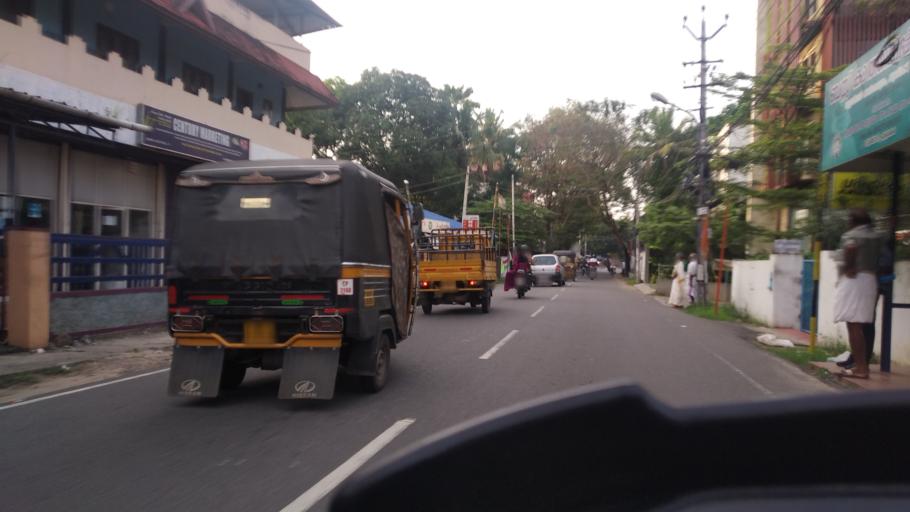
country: IN
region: Kerala
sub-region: Ernakulam
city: Elur
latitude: 10.0128
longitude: 76.2864
